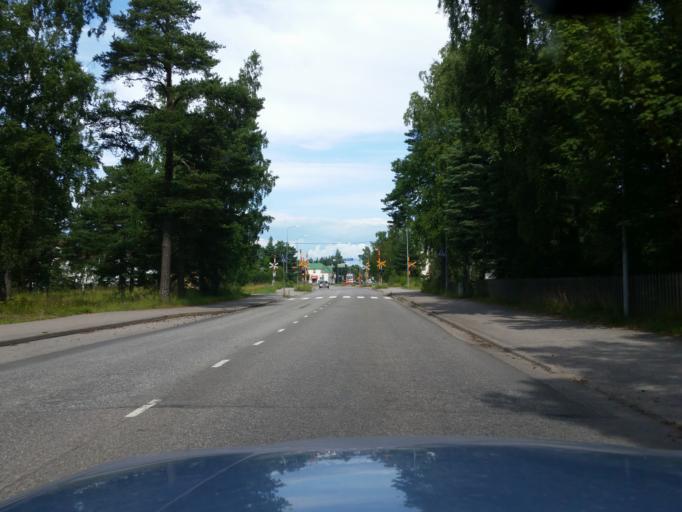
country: FI
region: Uusimaa
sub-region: Raaseporin
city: Hanko
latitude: 59.8296
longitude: 22.9894
